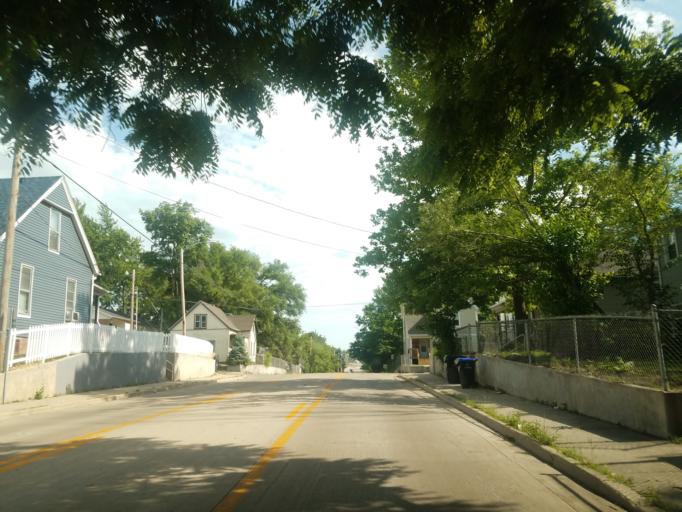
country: US
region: Illinois
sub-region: McLean County
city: Bloomington
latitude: 40.4780
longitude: -89.0066
